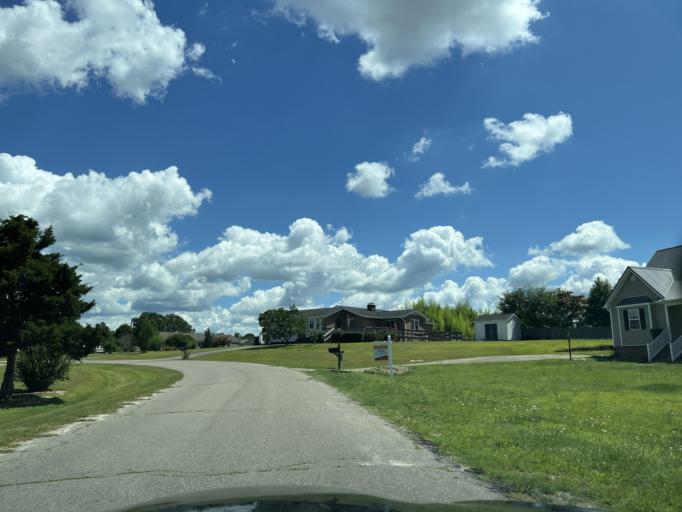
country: US
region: North Carolina
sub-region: Lee County
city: Sanford
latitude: 35.4322
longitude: -79.1605
